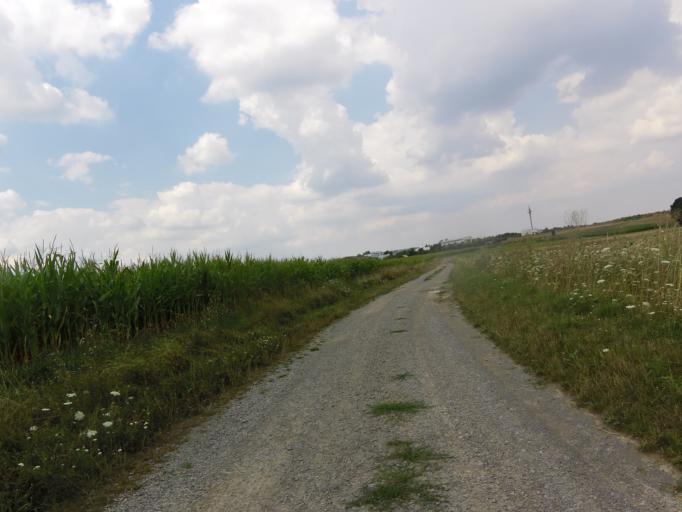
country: DE
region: Bavaria
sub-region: Regierungsbezirk Unterfranken
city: Eibelstadt
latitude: 49.7283
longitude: 9.9741
